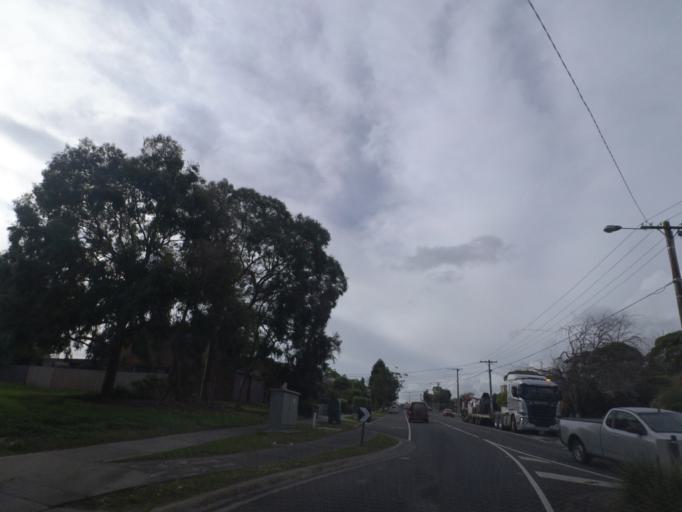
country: AU
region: Victoria
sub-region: Whitehorse
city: Vermont South
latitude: -37.8591
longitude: 145.1826
